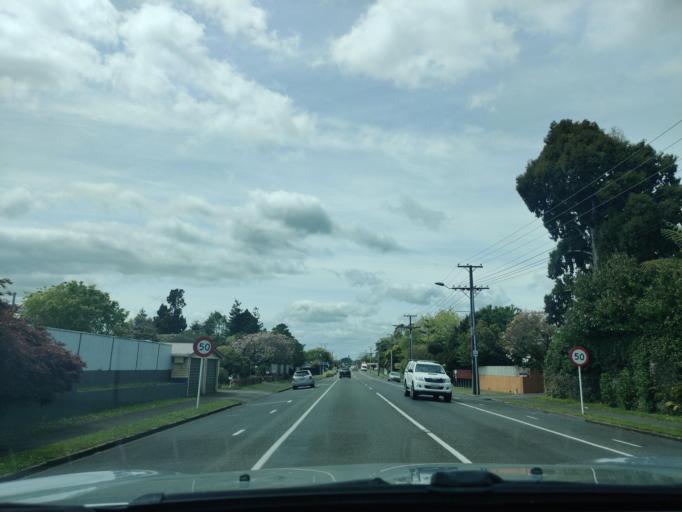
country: NZ
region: Taranaki
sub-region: New Plymouth District
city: New Plymouth
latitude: -39.1546
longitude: 174.1961
